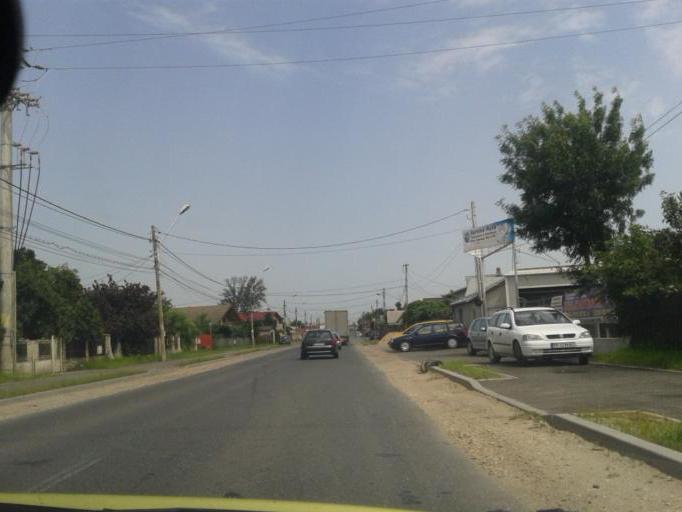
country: RO
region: Dambovita
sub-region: Oras Gaesti
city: Gaesti
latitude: 44.7074
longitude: 25.3098
